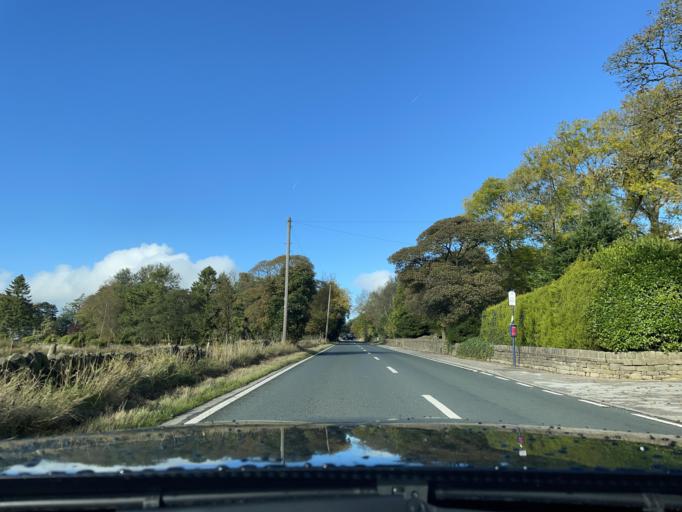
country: GB
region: England
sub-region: Sheffield
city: Bradfield
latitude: 53.3883
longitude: -1.6344
